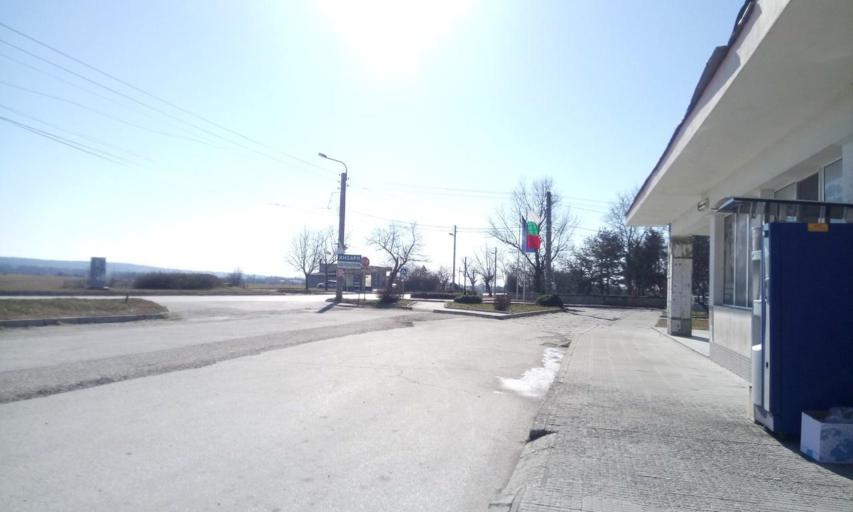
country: BG
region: Plovdiv
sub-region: Obshtina Khisarya
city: Khisarya
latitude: 42.5155
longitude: 24.7189
